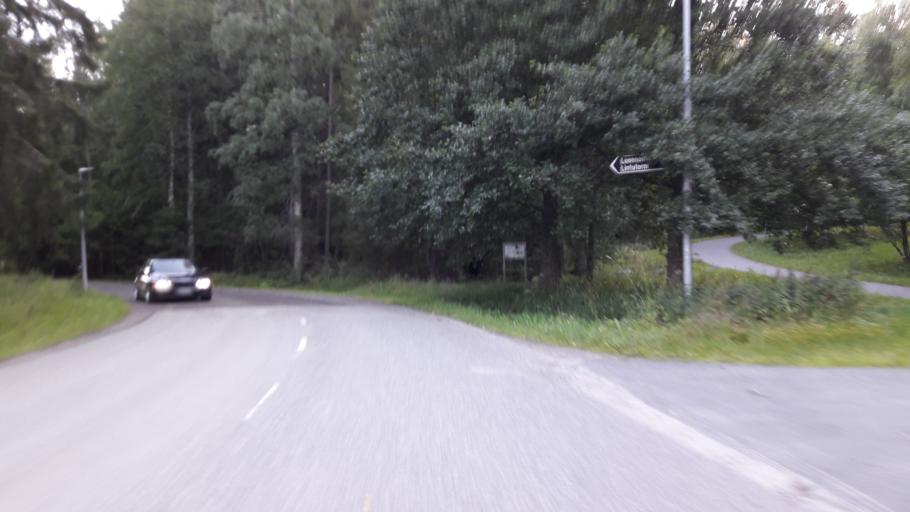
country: FI
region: North Karelia
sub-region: Joensuu
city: Joensuu
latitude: 62.6157
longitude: 29.7005
